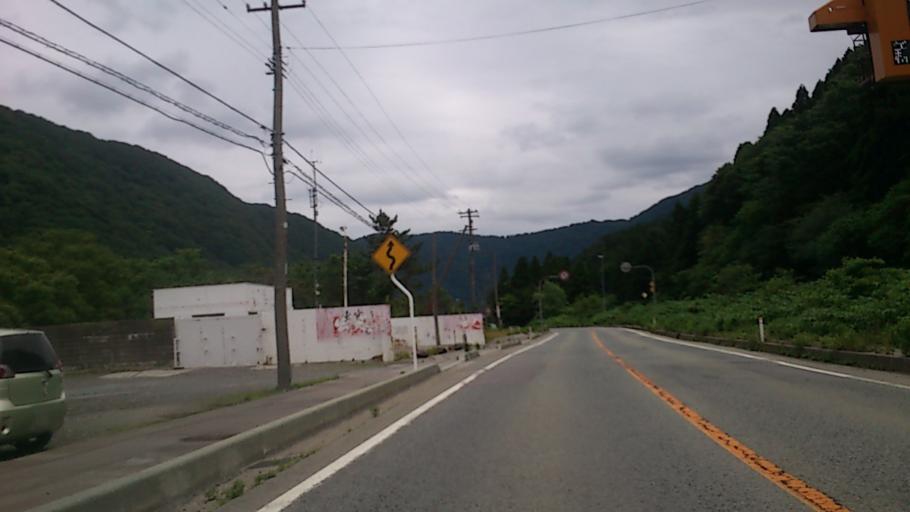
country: JP
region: Yamagata
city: Tsuruoka
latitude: 38.7643
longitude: 140.0563
